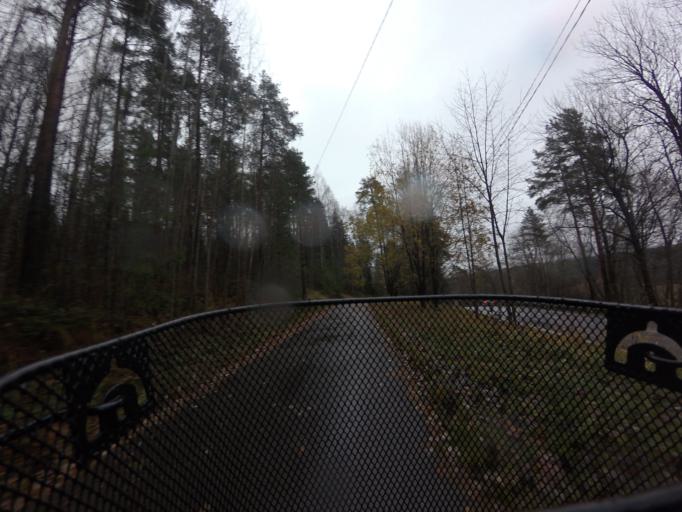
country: FI
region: Uusimaa
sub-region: Helsinki
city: Espoo
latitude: 60.1974
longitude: 24.6182
